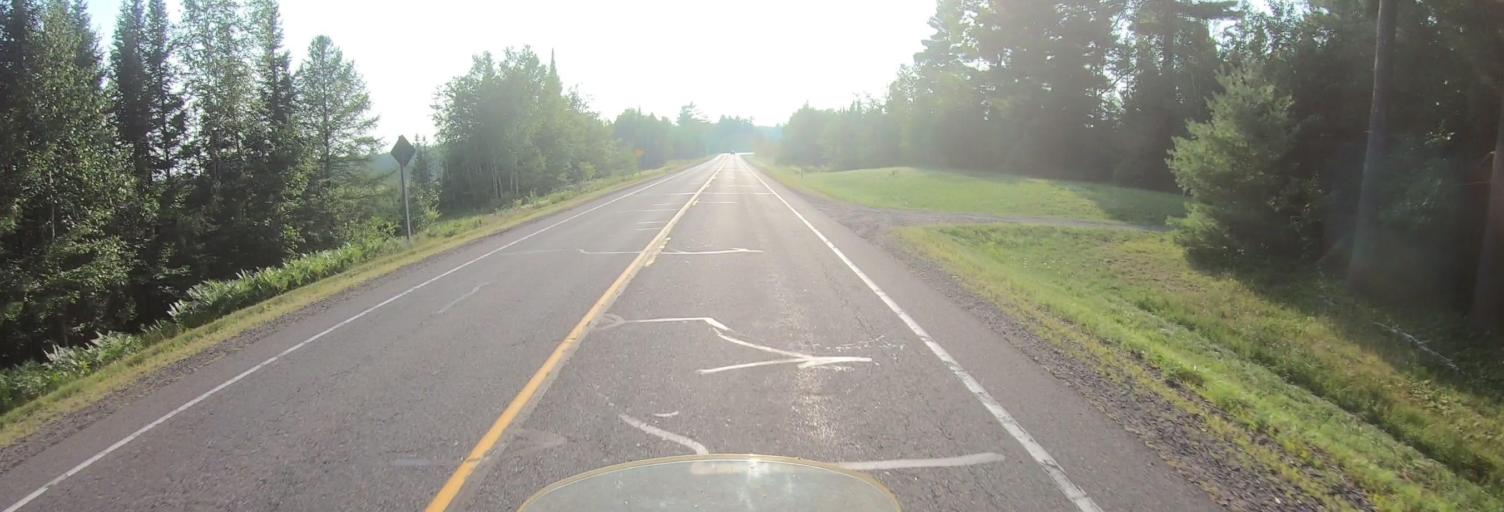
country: US
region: Wisconsin
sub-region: Sawyer County
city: Little Round Lake
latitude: 46.0633
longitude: -91.2134
